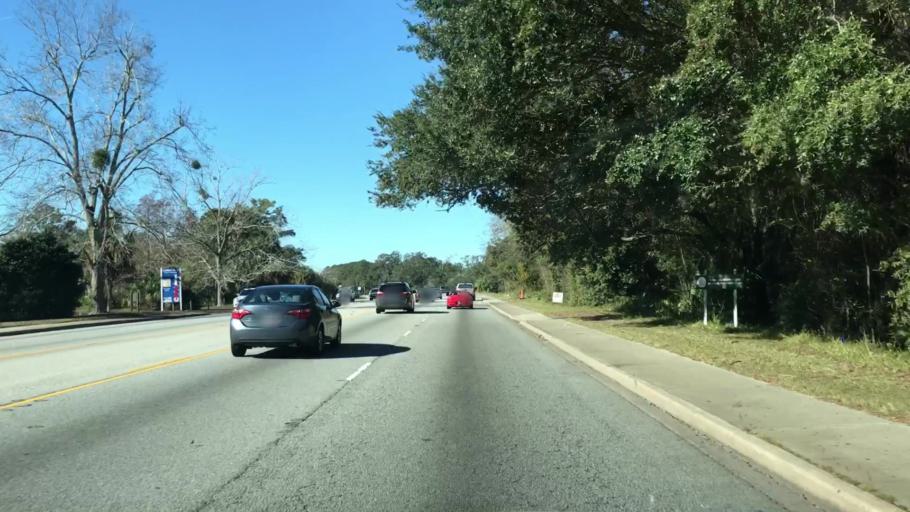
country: US
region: South Carolina
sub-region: Beaufort County
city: Hilton Head Island
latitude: 32.2177
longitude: -80.7592
